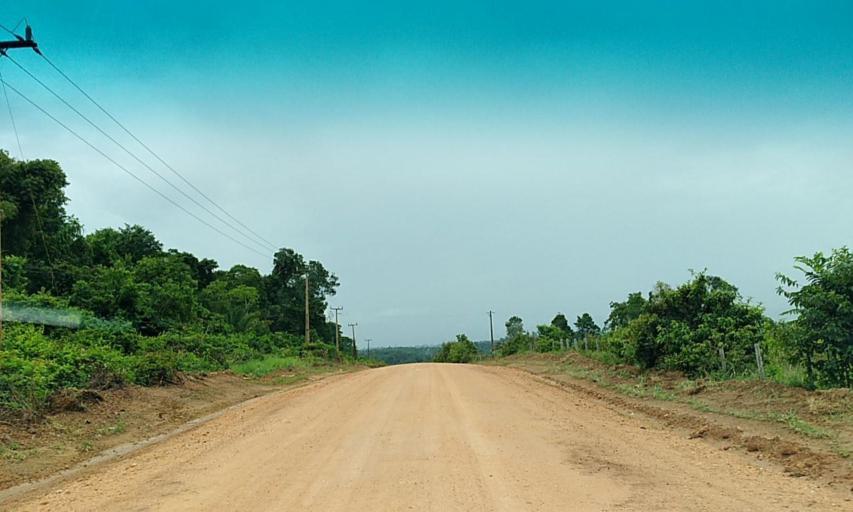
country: BR
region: Para
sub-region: Senador Jose Porfirio
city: Senador Jose Porfirio
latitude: -3.0594
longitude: -51.6527
